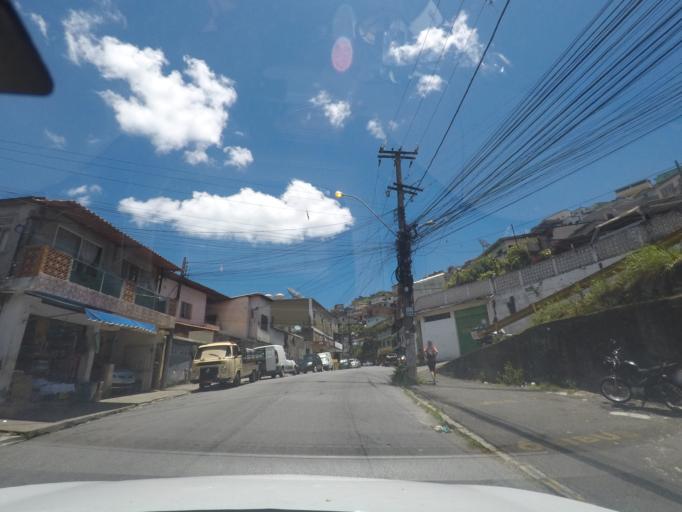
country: BR
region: Rio de Janeiro
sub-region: Teresopolis
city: Teresopolis
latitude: -22.4302
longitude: -42.9688
